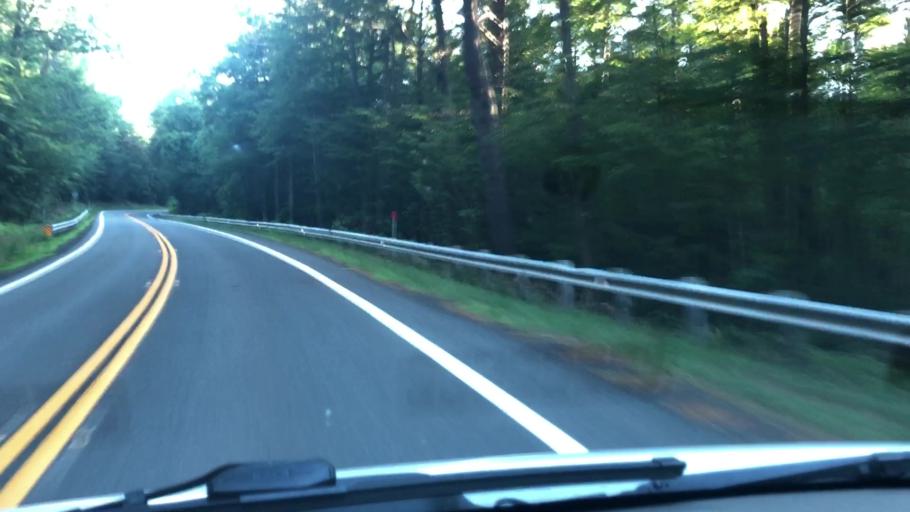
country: US
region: Massachusetts
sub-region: Hampshire County
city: Westhampton
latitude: 42.2893
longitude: -72.8707
